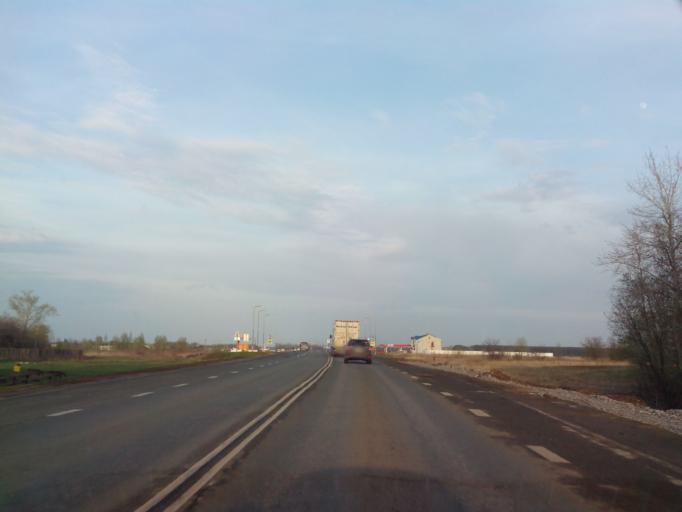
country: RU
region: Rjazan
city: Zarechnyy
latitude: 53.7524
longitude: 39.8033
